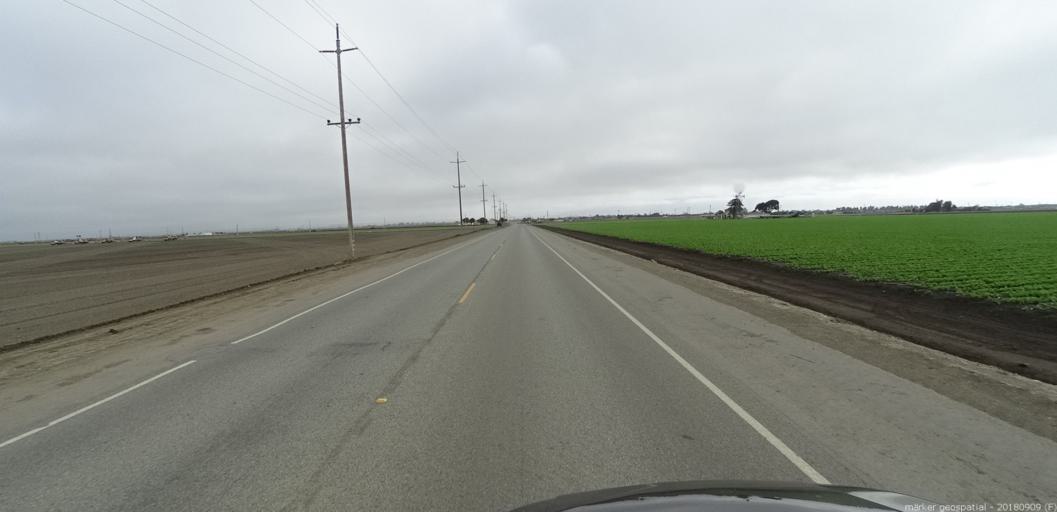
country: US
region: California
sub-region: Monterey County
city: Salinas
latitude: 36.6550
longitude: -121.6951
